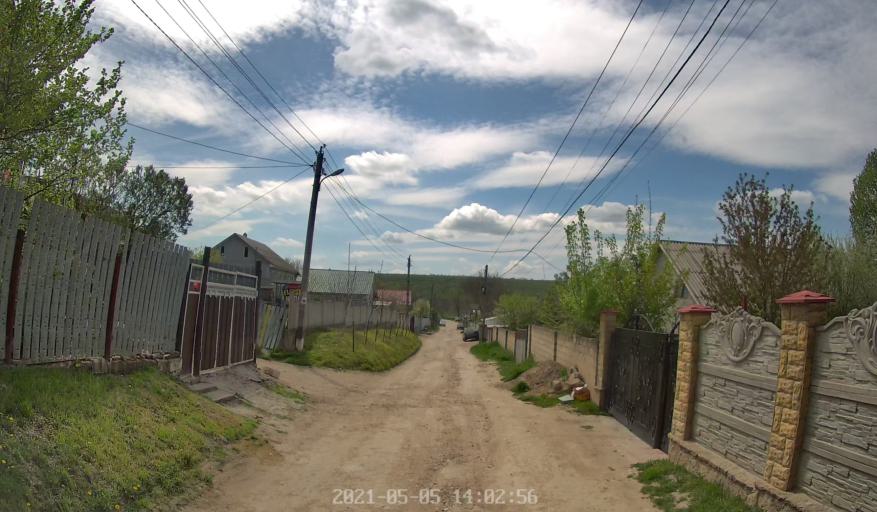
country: MD
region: Chisinau
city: Vadul lui Voda
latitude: 47.0639
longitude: 29.1365
